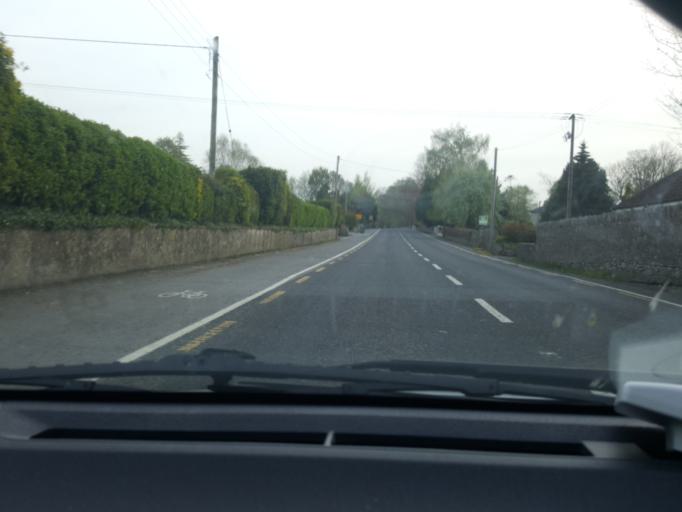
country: IE
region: Munster
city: Cahir
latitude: 52.3846
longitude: -7.9159
